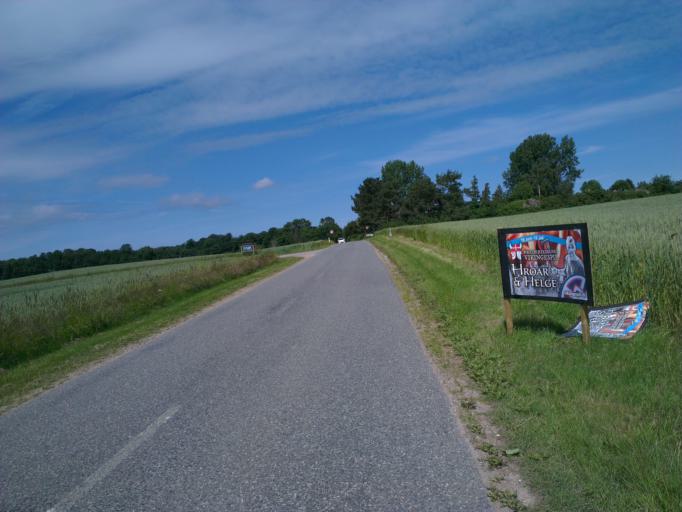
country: DK
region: Capital Region
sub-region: Frederikssund Kommune
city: Jaegerspris
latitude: 55.8098
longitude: 11.9330
